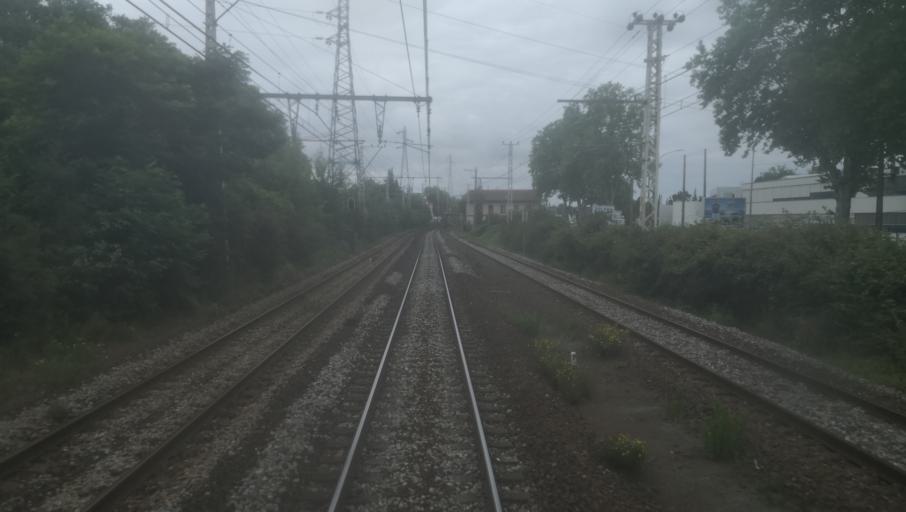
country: FR
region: Midi-Pyrenees
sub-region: Departement de la Haute-Garonne
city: Aucamville
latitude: 43.6651
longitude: 1.4128
